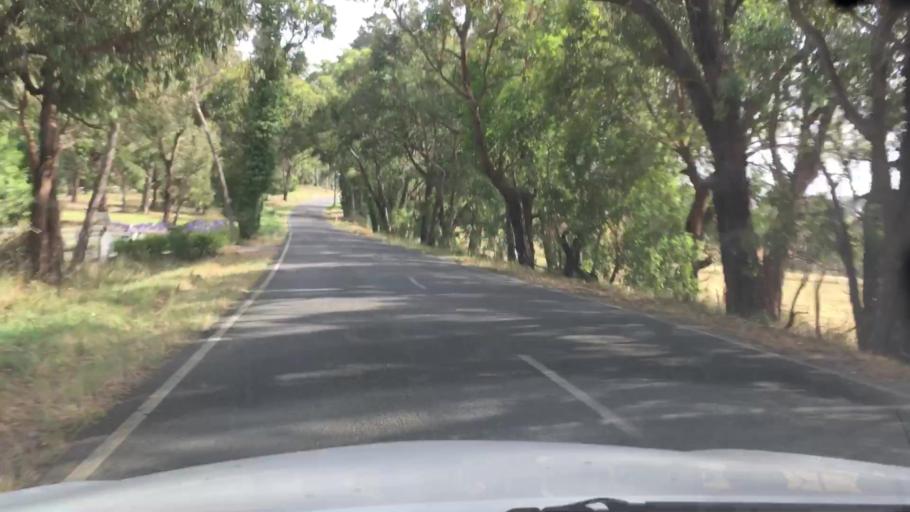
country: AU
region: Victoria
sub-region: Yarra Ranges
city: Macclesfield
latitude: -37.8740
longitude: 145.4786
